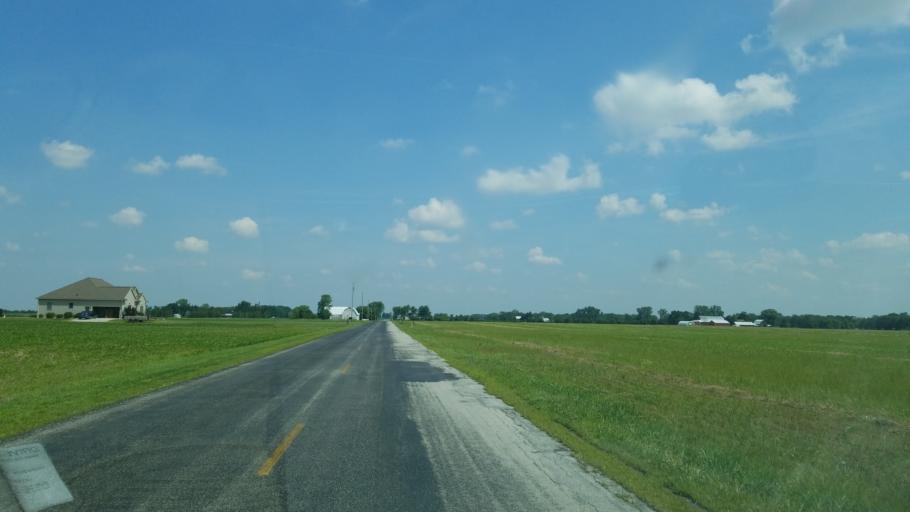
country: US
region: Ohio
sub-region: Seneca County
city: Fostoria
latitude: 41.2463
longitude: -83.5352
